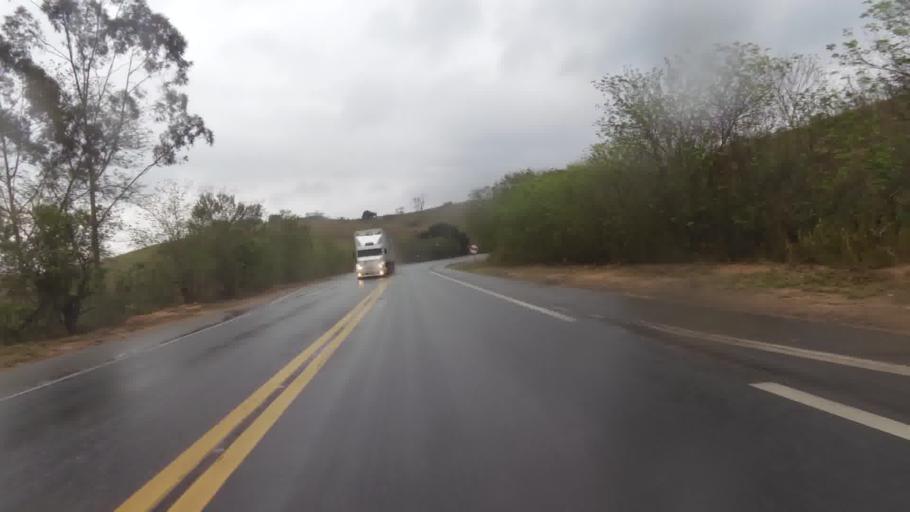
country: BR
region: Espirito Santo
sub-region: Rio Novo Do Sul
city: Rio Novo do Sul
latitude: -20.8989
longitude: -41.0220
